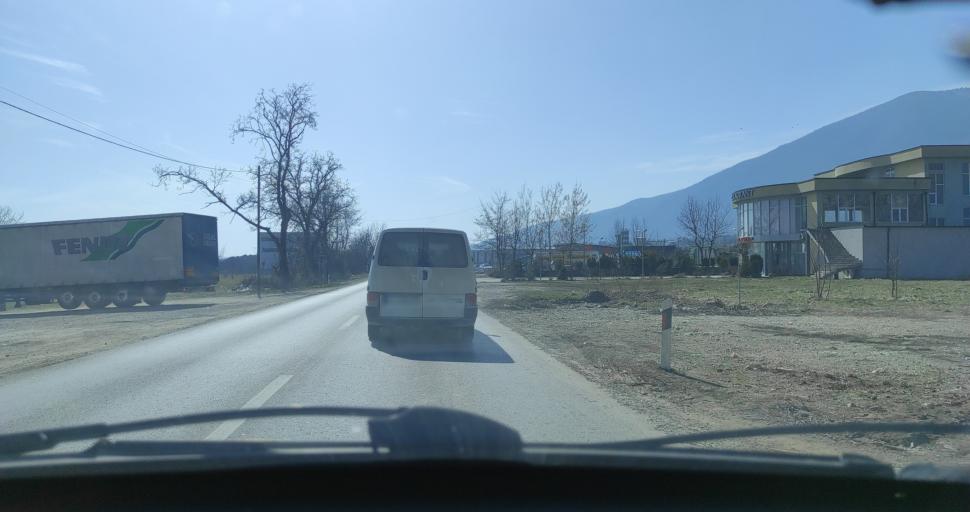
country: XK
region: Gjakova
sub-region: Komuna e Decanit
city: Strellc i Ulet
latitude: 42.6134
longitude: 20.3026
